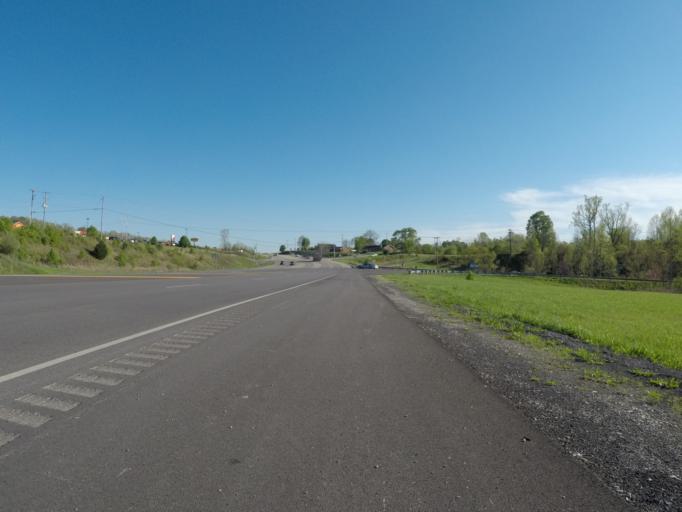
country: US
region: Kentucky
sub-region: Boyd County
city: Meads
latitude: 38.3664
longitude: -82.6990
